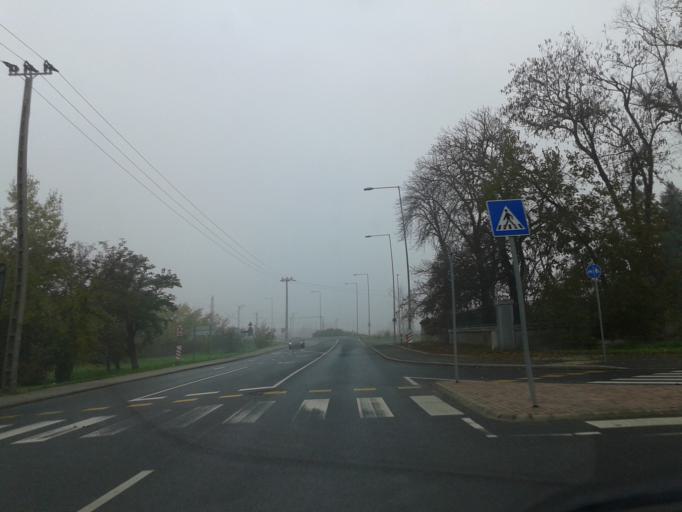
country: HU
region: Pest
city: Halasztelek
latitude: 47.3882
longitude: 18.9724
